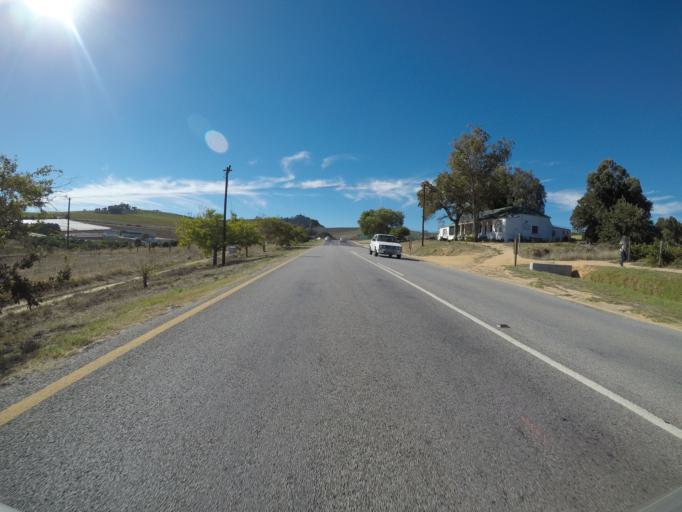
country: ZA
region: Western Cape
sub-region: City of Cape Town
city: Kraaifontein
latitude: -33.9647
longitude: 18.7445
